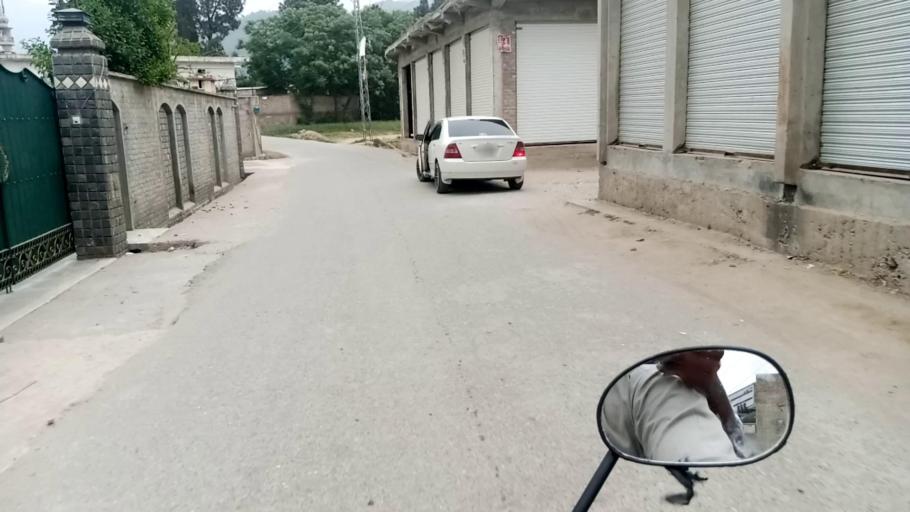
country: PK
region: Khyber Pakhtunkhwa
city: Saidu Sharif
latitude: 34.7564
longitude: 72.3803
